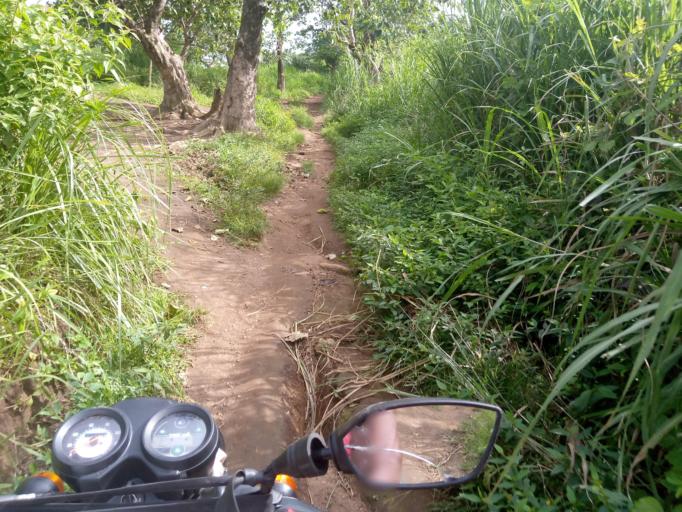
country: SL
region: Eastern Province
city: Buedu
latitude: 8.4553
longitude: -10.3350
